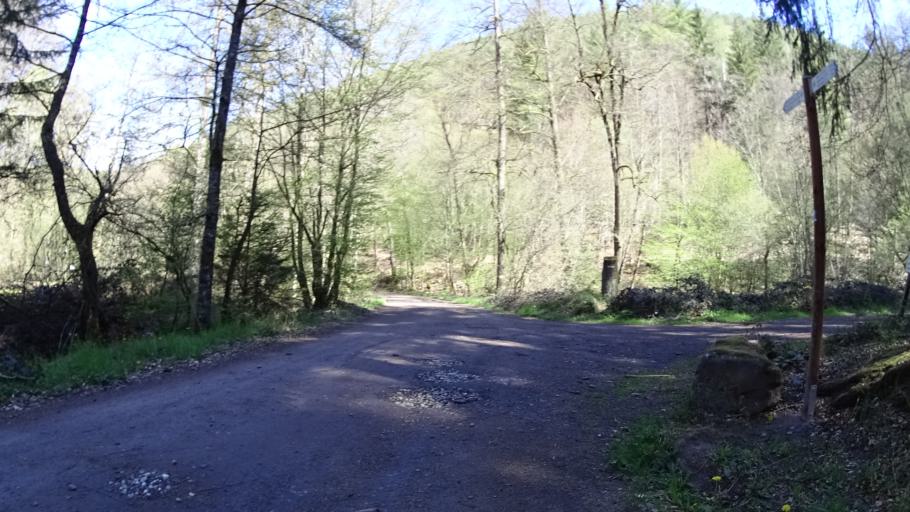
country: DE
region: Rheinland-Pfalz
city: Esthal
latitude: 49.3323
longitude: 7.9868
